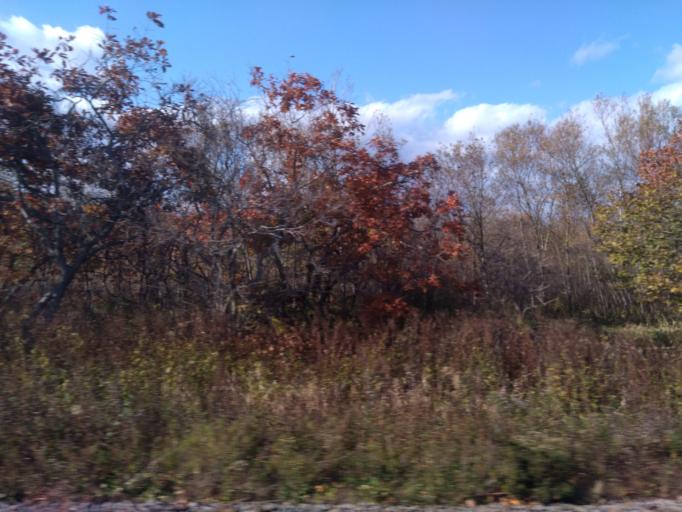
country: JP
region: Hokkaido
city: Shiraoi
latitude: 42.5371
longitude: 141.3312
